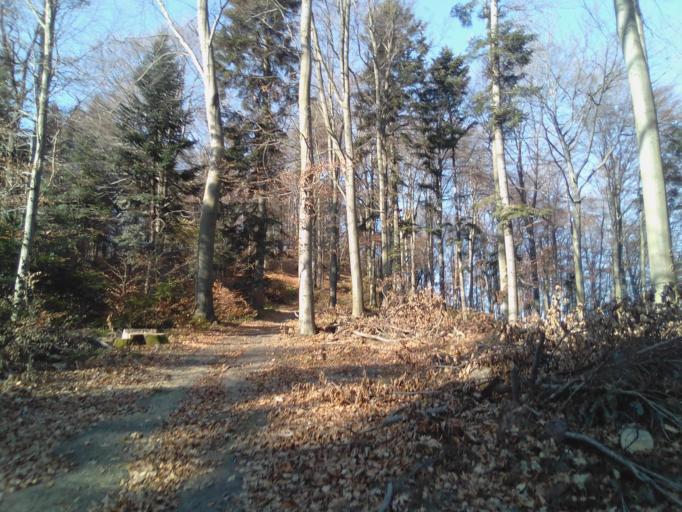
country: PL
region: Subcarpathian Voivodeship
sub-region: Powiat krosnienski
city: Leki
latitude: 49.8202
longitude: 21.7005
